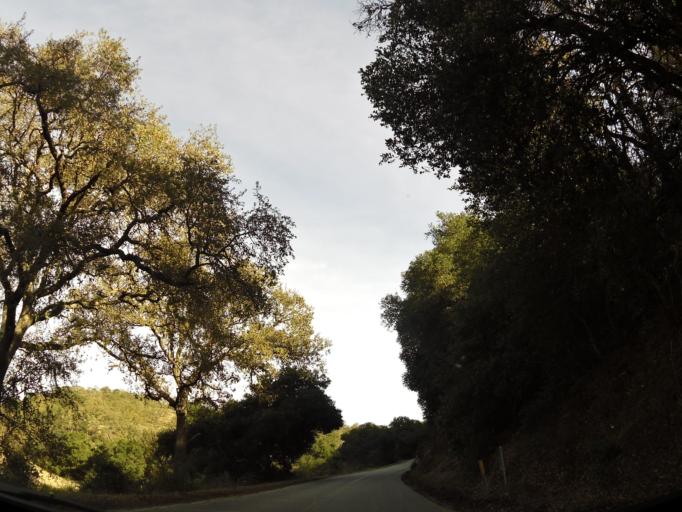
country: US
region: California
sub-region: San Benito County
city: Ridgemark
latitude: 36.7577
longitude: -121.3963
